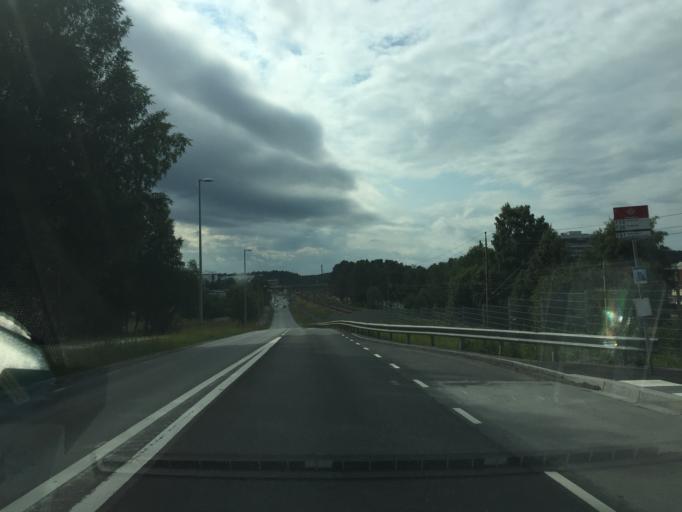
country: SE
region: Stockholm
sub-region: Botkyrka Kommun
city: Tumba
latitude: 59.1991
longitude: 17.8541
